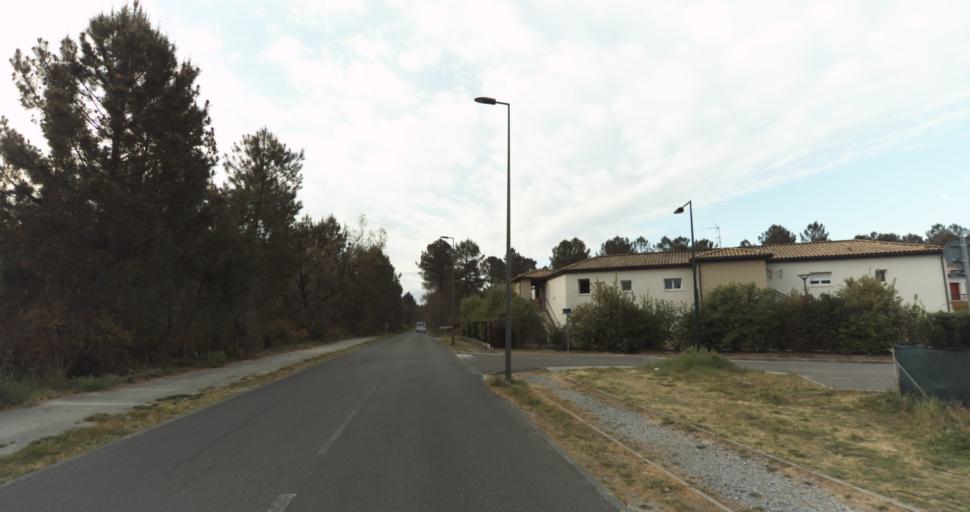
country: FR
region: Aquitaine
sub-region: Departement de la Gironde
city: Martignas-sur-Jalle
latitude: 44.8053
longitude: -0.7710
